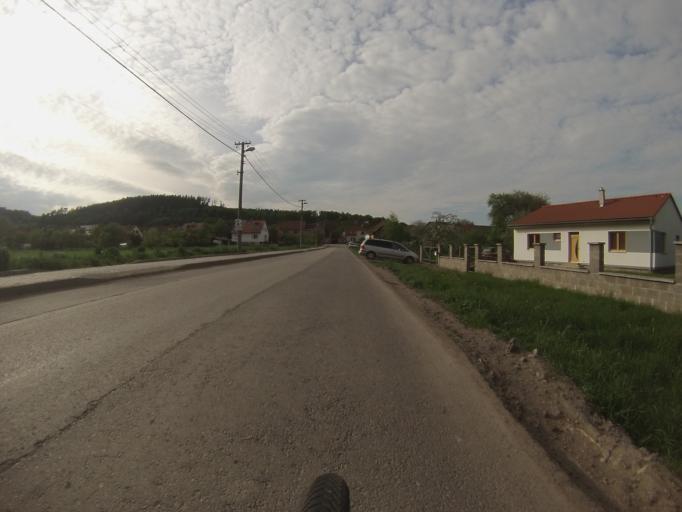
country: CZ
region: South Moravian
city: Cebin
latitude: 49.3132
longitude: 16.4531
